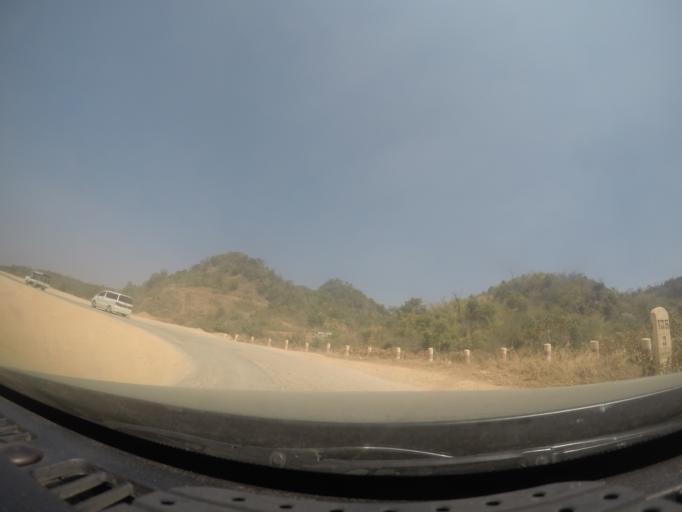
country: MM
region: Shan
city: Taunggyi
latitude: 20.8089
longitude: 97.2798
